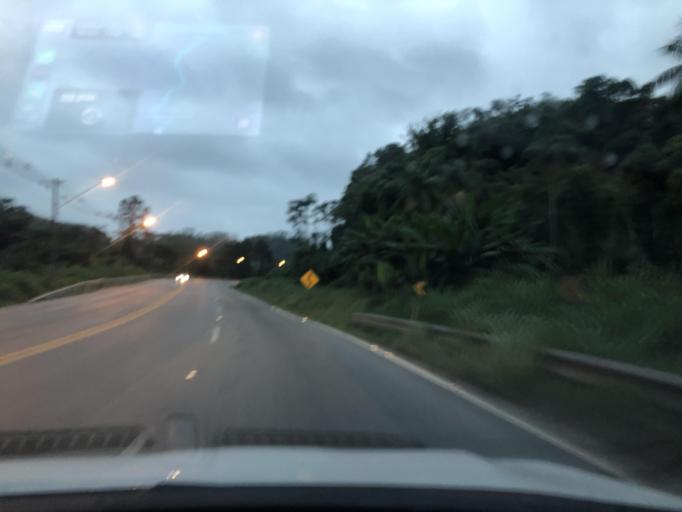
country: BR
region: Santa Catarina
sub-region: Pomerode
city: Pomerode
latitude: -26.7536
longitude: -49.0710
